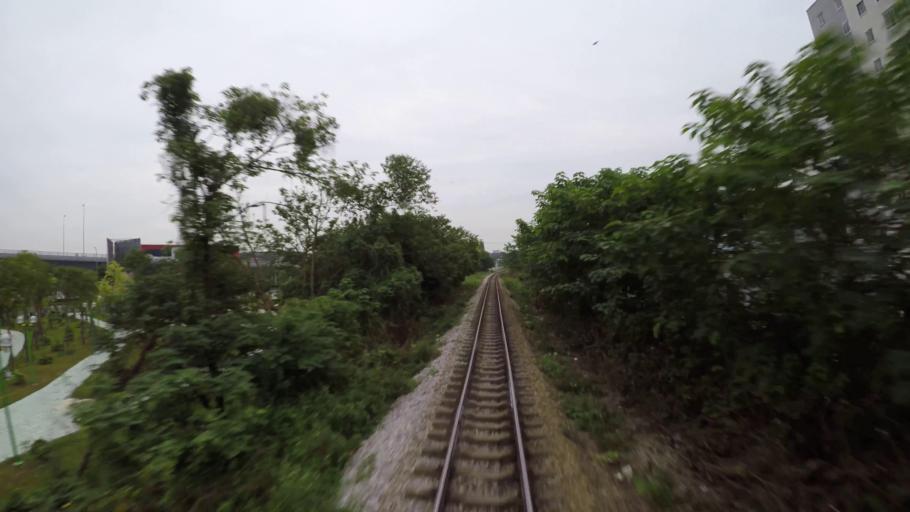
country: VN
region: Ha Noi
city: Trau Quy
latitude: 21.0183
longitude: 105.9419
